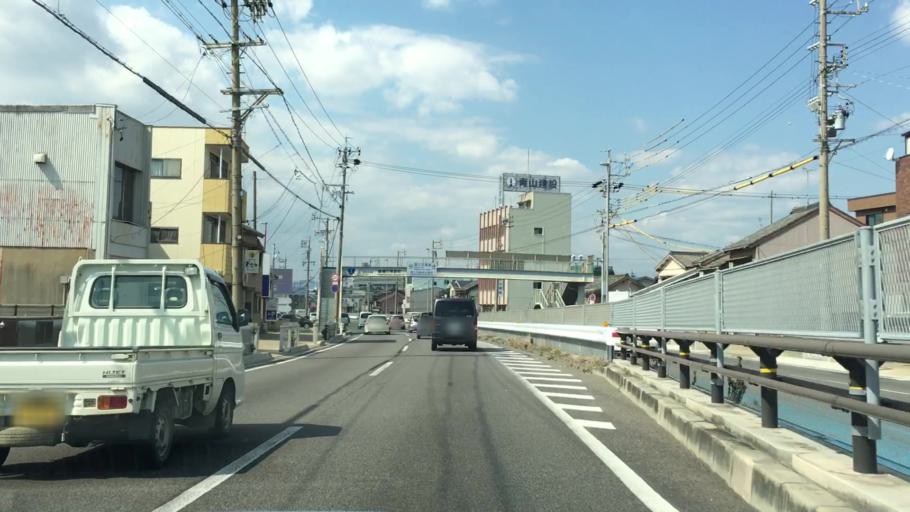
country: JP
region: Aichi
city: Toyohashi
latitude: 34.7632
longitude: 137.4038
